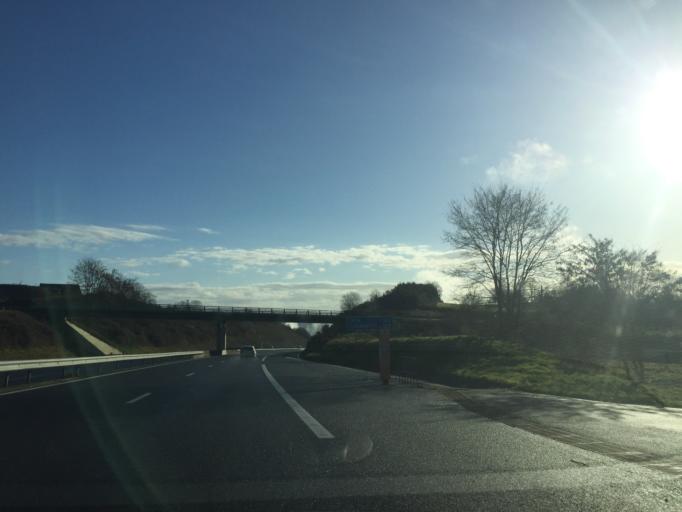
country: FR
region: Limousin
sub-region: Departement de la Correze
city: Naves
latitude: 45.3273
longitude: 1.7672
